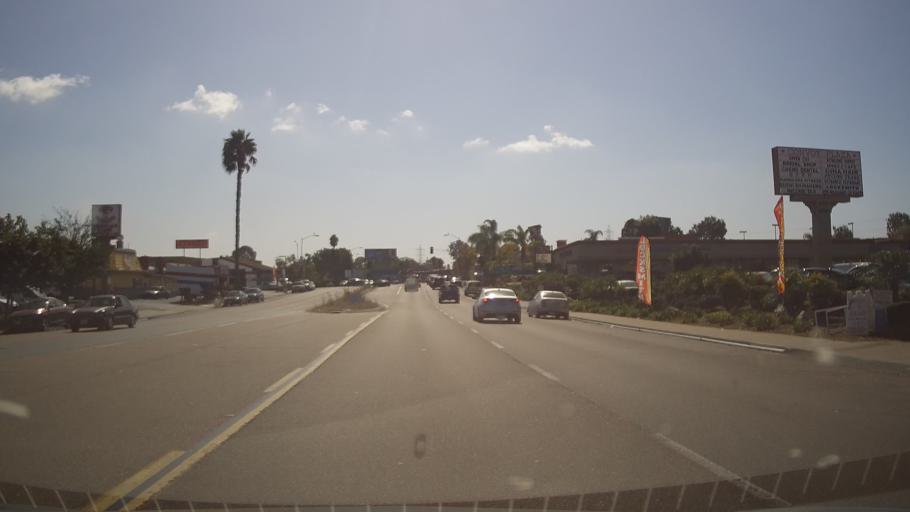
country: US
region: California
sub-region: San Diego County
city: San Diego
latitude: 32.8186
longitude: -117.1550
